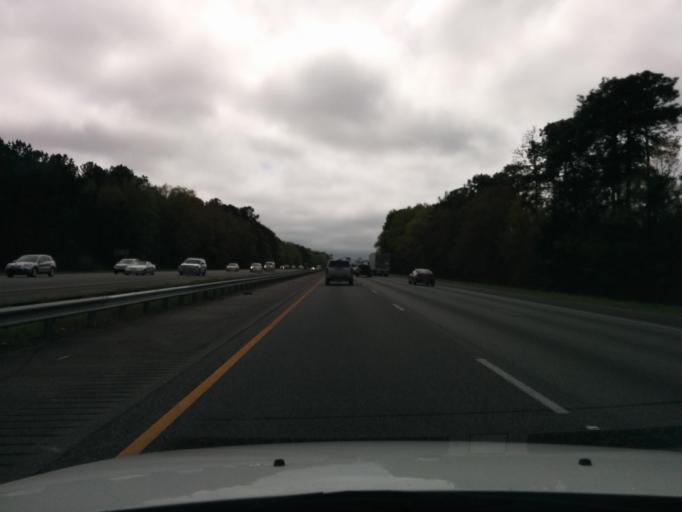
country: US
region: Georgia
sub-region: Chatham County
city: Georgetown
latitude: 32.0177
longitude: -81.2745
